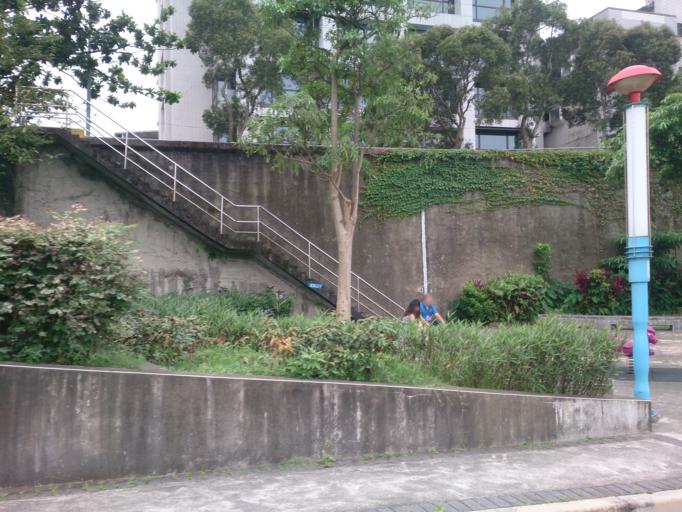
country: TW
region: Taipei
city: Taipei
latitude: 25.0541
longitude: 121.5865
